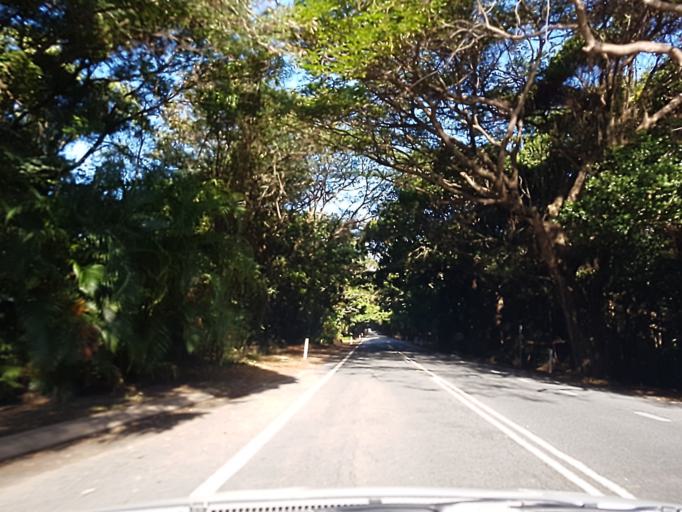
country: AU
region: Queensland
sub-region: Cairns
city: Palm Cove
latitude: -16.7267
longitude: 145.6468
